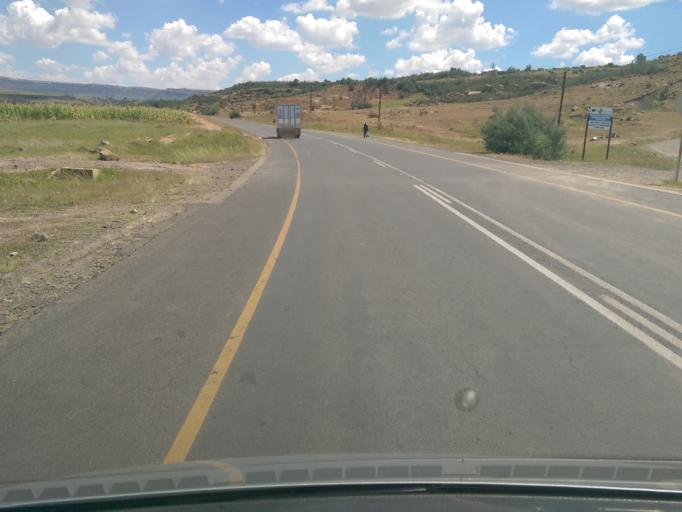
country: LS
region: Maseru
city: Maseru
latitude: -29.3928
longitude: 27.5437
